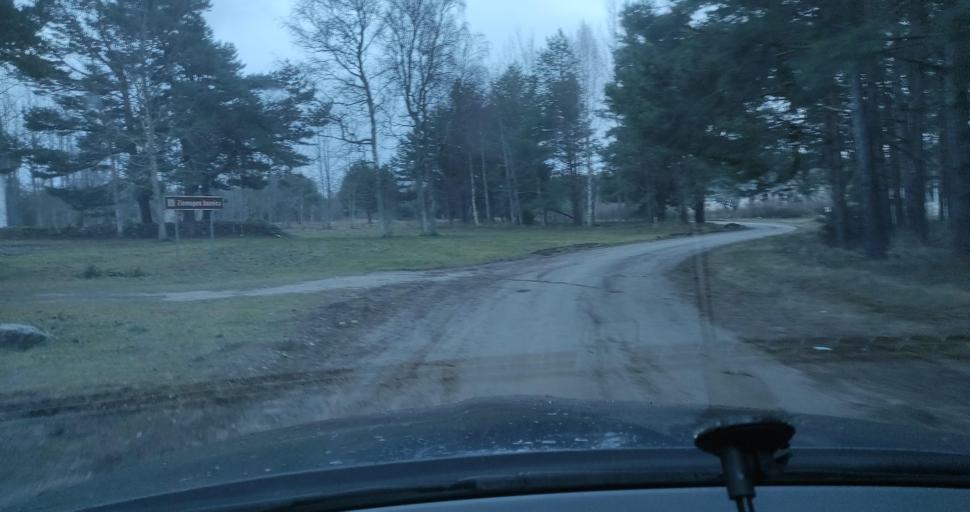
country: LV
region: Pavilostas
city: Pavilosta
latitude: 56.7413
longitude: 21.0676
